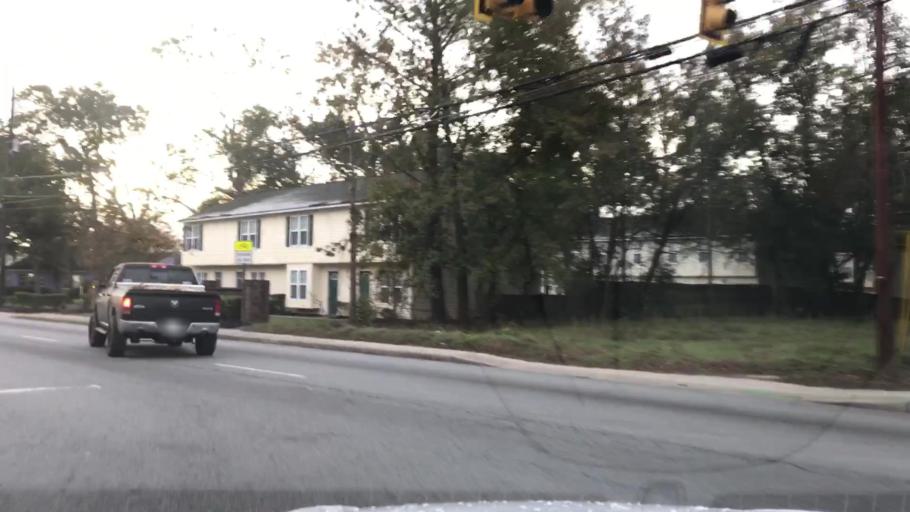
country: US
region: South Carolina
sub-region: Charleston County
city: North Charleston
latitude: 32.7987
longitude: -80.0060
